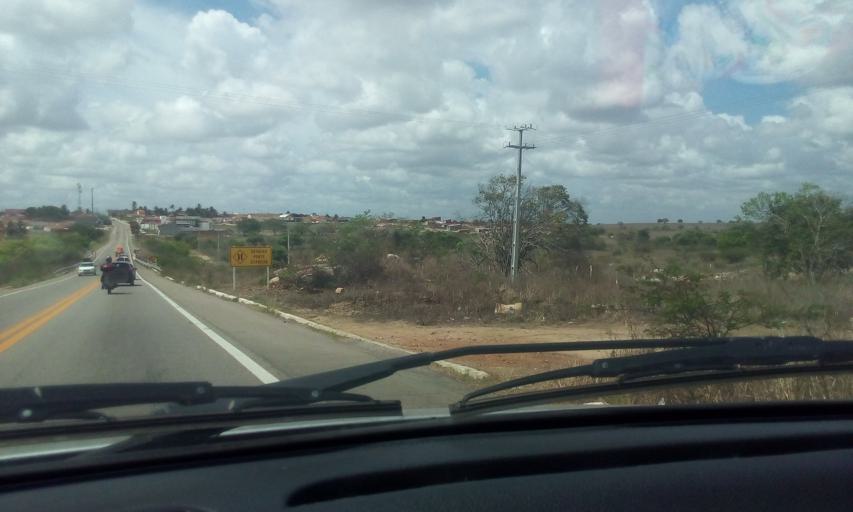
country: BR
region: Rio Grande do Norte
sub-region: Sao Paulo Do Potengi
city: Sao Paulo do Potengi
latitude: -5.9786
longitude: -35.5763
